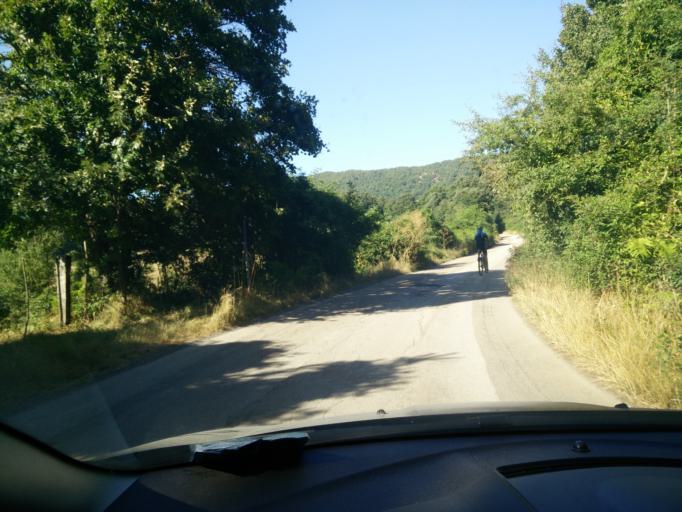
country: IT
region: Apulia
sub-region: Provincia di Foggia
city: Monte Sant'Angelo
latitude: 41.7686
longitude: 15.9837
